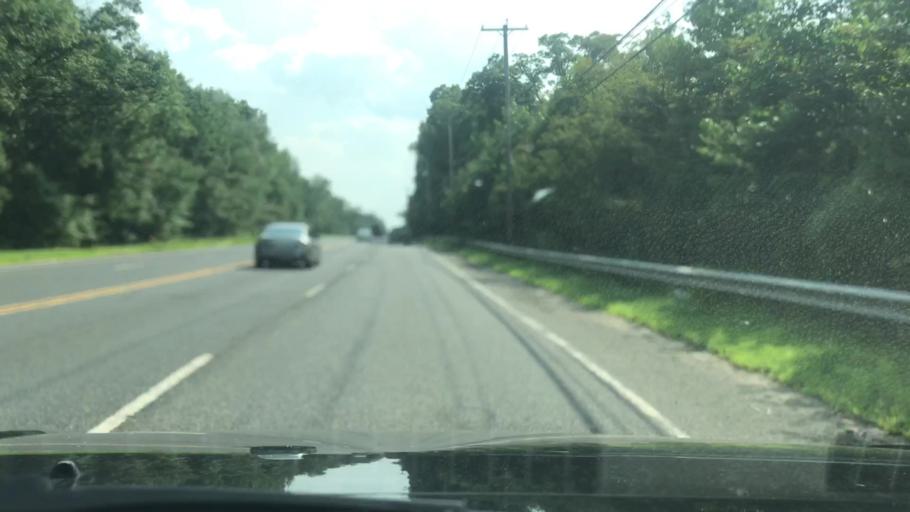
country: US
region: New Jersey
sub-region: Monmouth County
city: Tinton Falls
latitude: 40.2349
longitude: -74.1098
